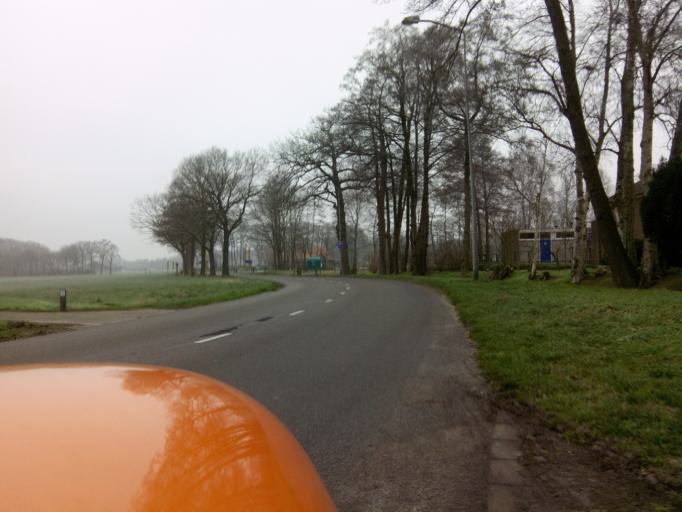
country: NL
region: Gelderland
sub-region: Gemeente Barneveld
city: Voorthuizen
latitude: 52.1916
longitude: 5.6035
